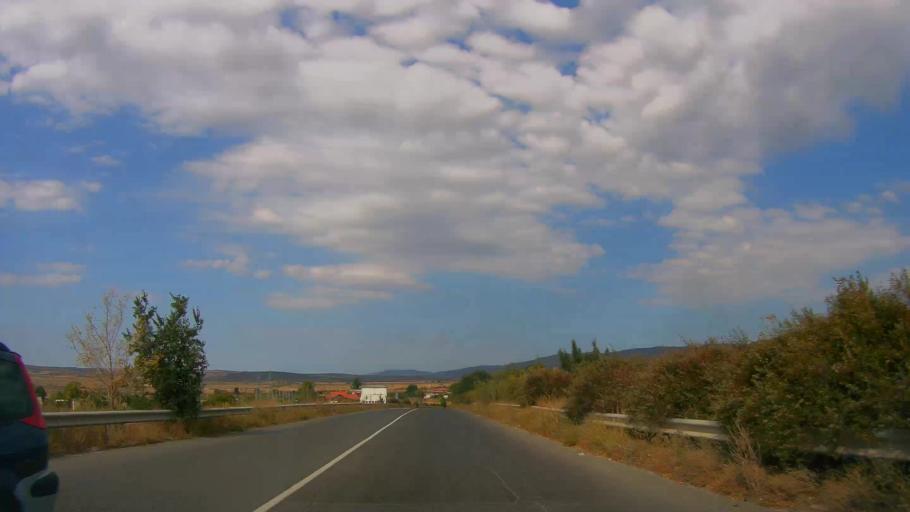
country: BG
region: Burgas
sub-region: Obshtina Aytos
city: Aytos
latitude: 42.7041
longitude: 27.2411
